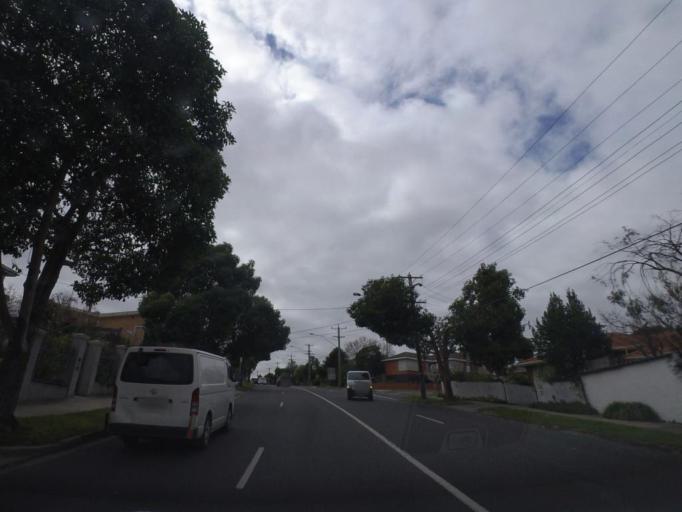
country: AU
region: Victoria
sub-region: Manningham
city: Doncaster
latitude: -37.7944
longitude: 145.1201
